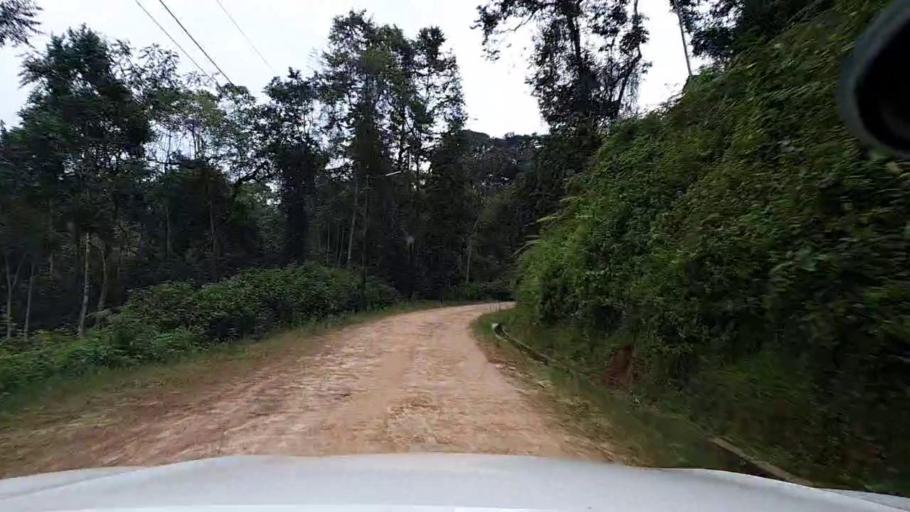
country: RW
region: Western Province
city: Cyangugu
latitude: -2.5647
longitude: 29.2303
